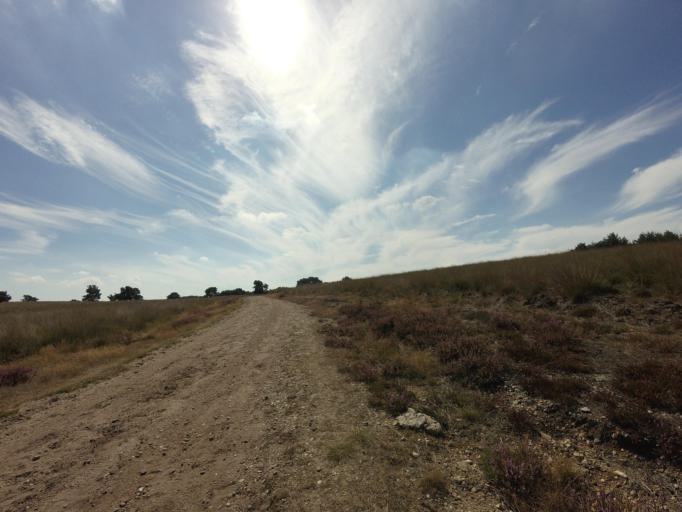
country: NL
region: Gelderland
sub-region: Gemeente Rheden
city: Rheden
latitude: 52.0476
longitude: 5.9996
